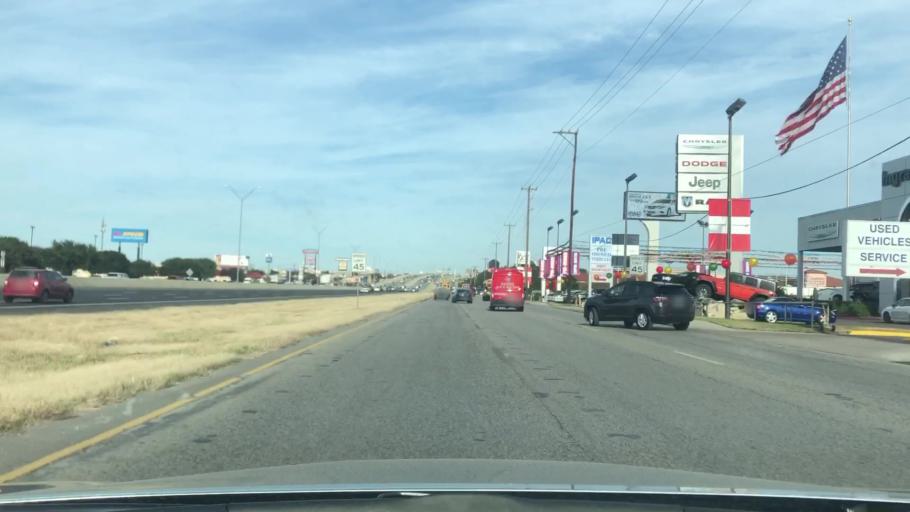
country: US
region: Texas
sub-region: Bexar County
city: Leon Valley
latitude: 29.4566
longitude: -98.6268
